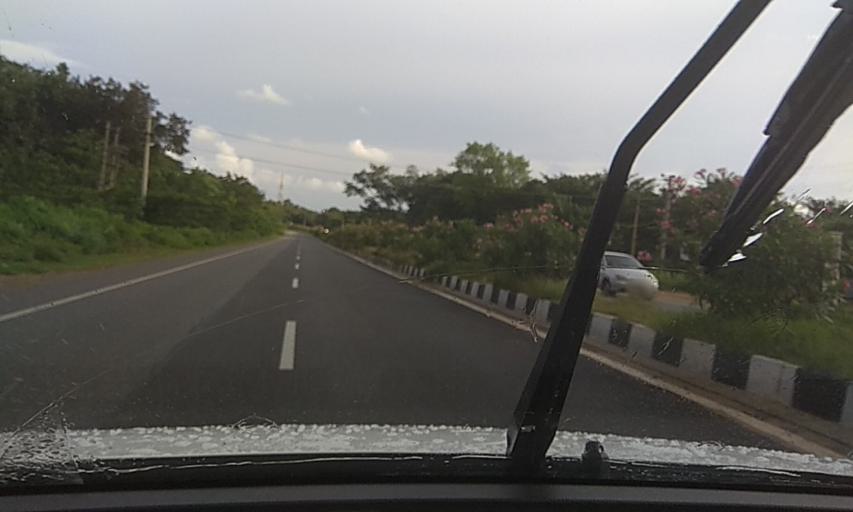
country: IN
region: Karnataka
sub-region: Mysore
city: Nanjangud
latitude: 12.1724
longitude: 76.6725
